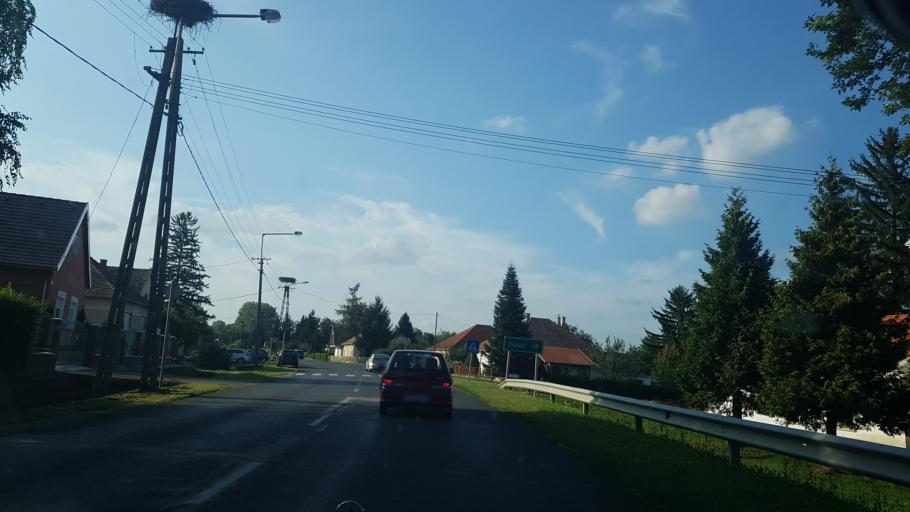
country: HU
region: Somogy
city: Segesd
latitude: 46.2873
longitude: 17.3609
